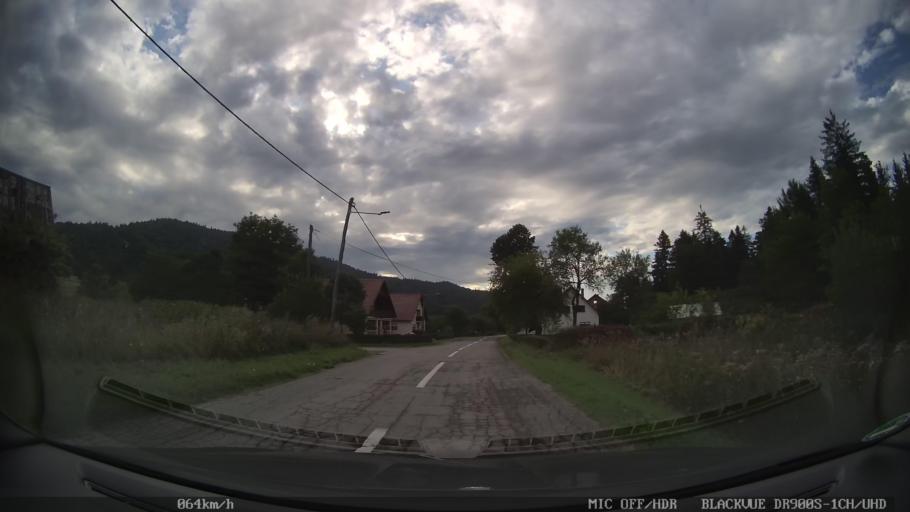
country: HR
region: Licko-Senjska
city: Jezerce
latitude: 44.9478
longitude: 15.5372
